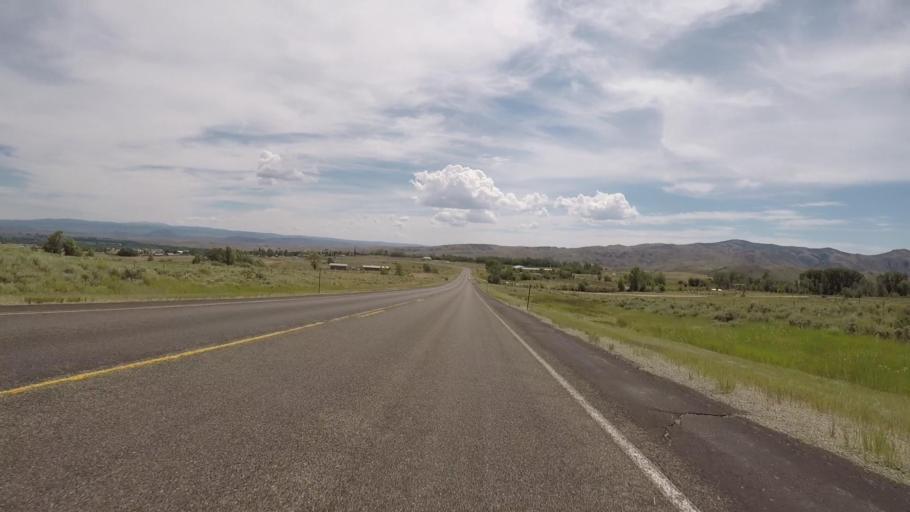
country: US
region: Wyoming
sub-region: Carbon County
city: Saratoga
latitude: 41.2056
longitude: -106.8119
